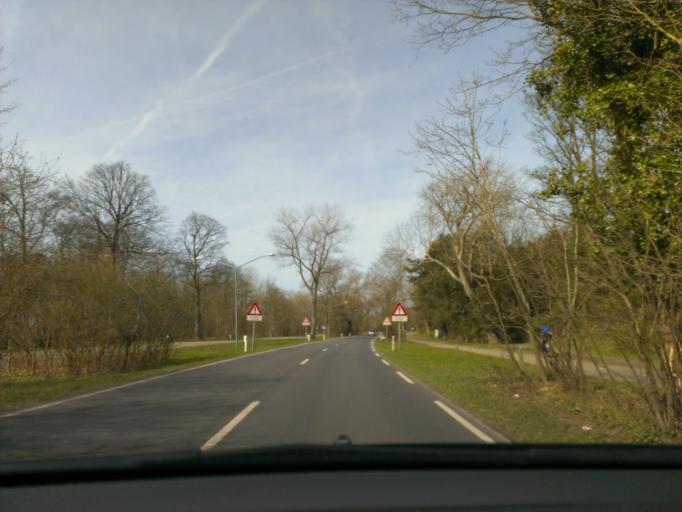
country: NL
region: North Holland
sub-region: Gemeente Bloemendaal
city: Bloemendaal
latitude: 52.3949
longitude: 4.5913
